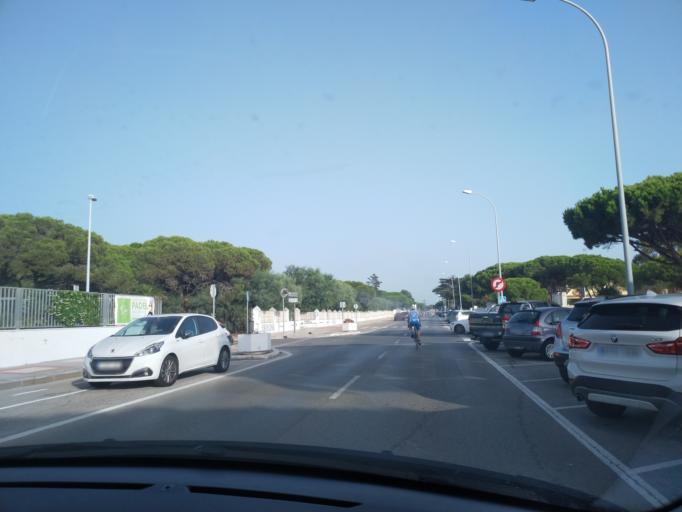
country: ES
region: Andalusia
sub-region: Provincia de Cadiz
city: Chiclana de la Frontera
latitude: 36.3742
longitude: -6.1843
